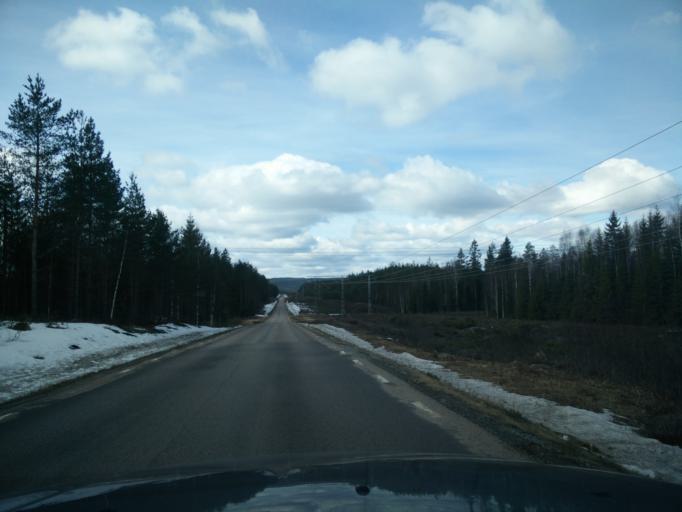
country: SE
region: Vaermland
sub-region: Hagfors Kommun
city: Hagfors
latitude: 60.0352
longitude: 13.5589
